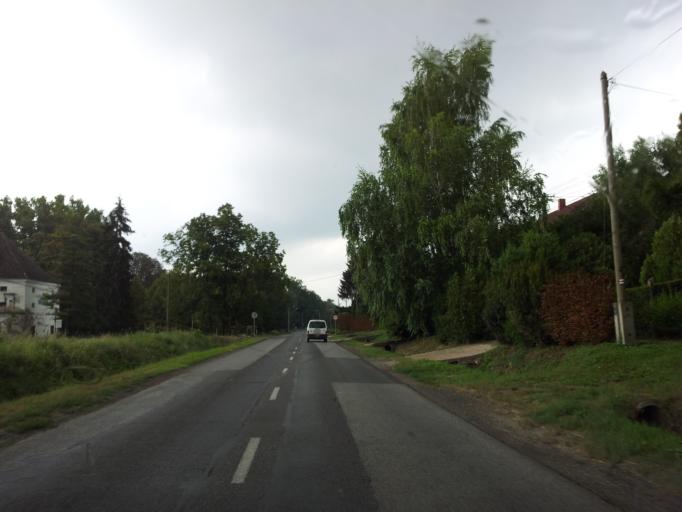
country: HU
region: Tolna
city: Hogyesz
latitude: 46.5022
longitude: 18.4136
